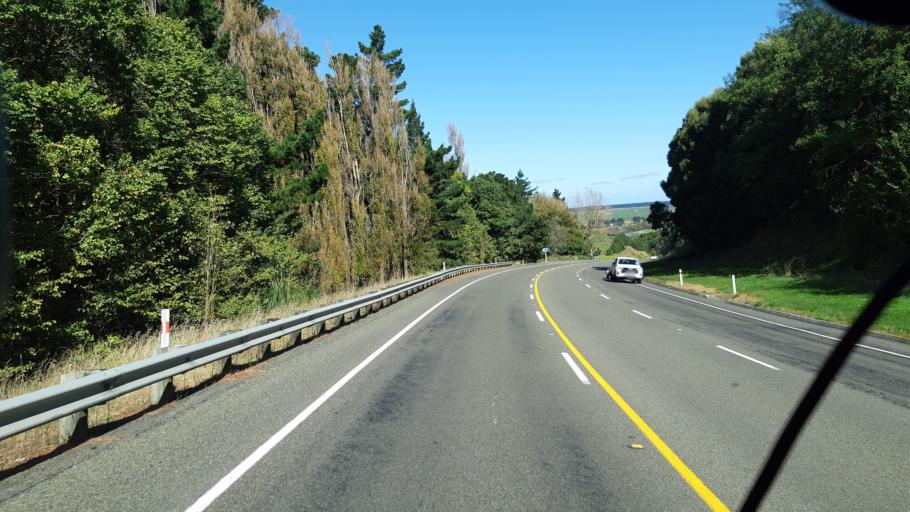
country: NZ
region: Manawatu-Wanganui
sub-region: Wanganui District
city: Wanganui
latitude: -39.9965
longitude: 175.1690
